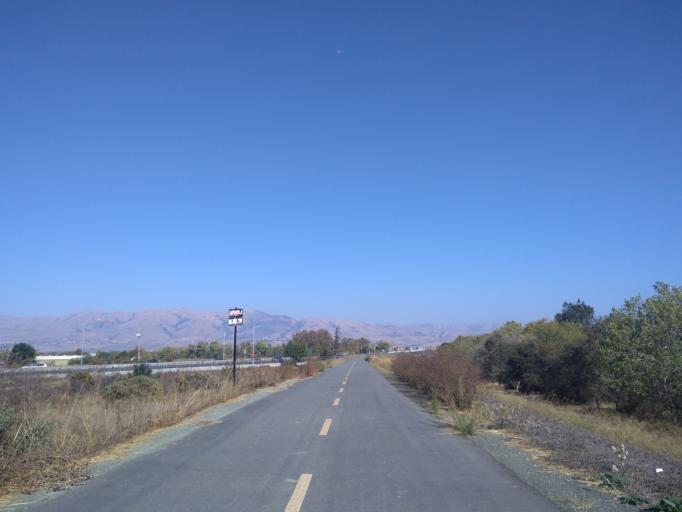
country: US
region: California
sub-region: Santa Clara County
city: Milpitas
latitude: 37.4214
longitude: -121.9303
